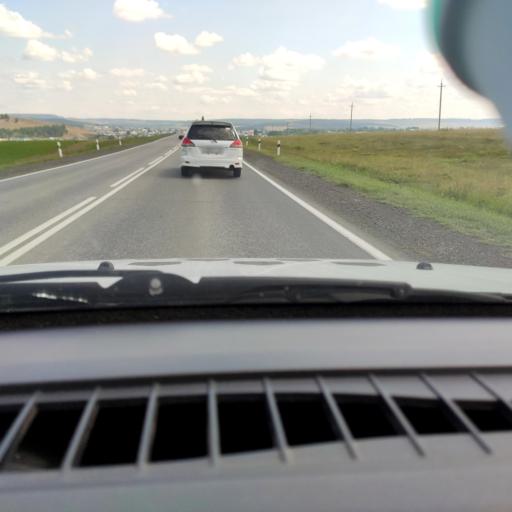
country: RU
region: Bashkortostan
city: Verkhniye Kigi
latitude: 55.4258
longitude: 58.5628
